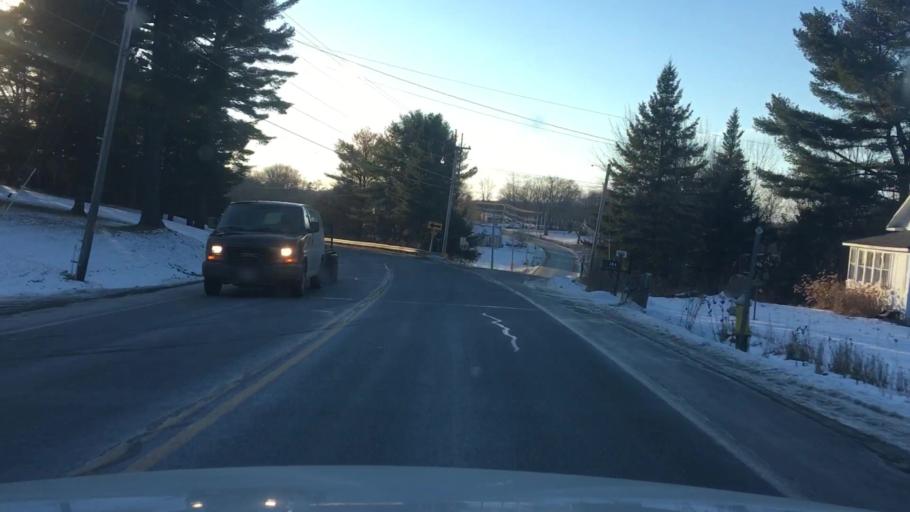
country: US
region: Maine
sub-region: Penobscot County
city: Eddington
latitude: 44.8275
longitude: -68.6881
